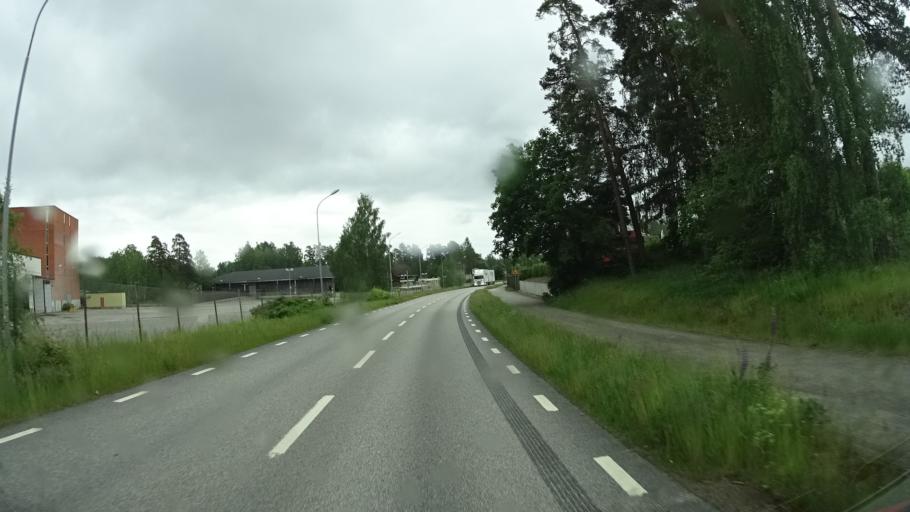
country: SE
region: Kalmar
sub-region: Hultsfreds Kommun
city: Hultsfred
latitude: 57.5425
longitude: 15.7533
